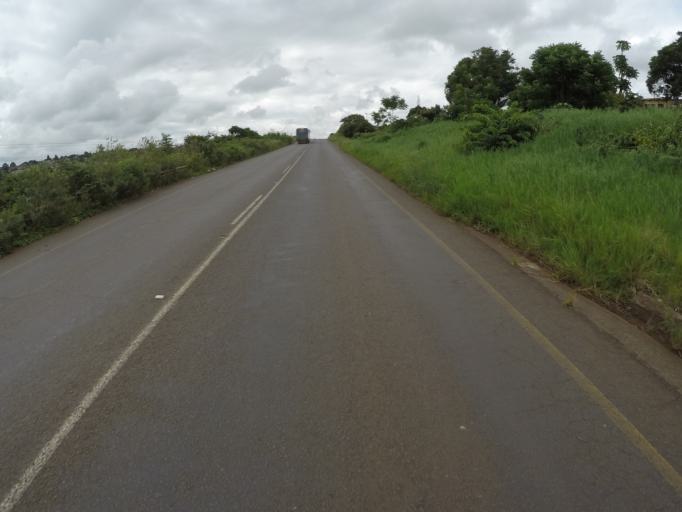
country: ZA
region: KwaZulu-Natal
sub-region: uThungulu District Municipality
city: Empangeni
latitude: -28.7755
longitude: 31.8763
